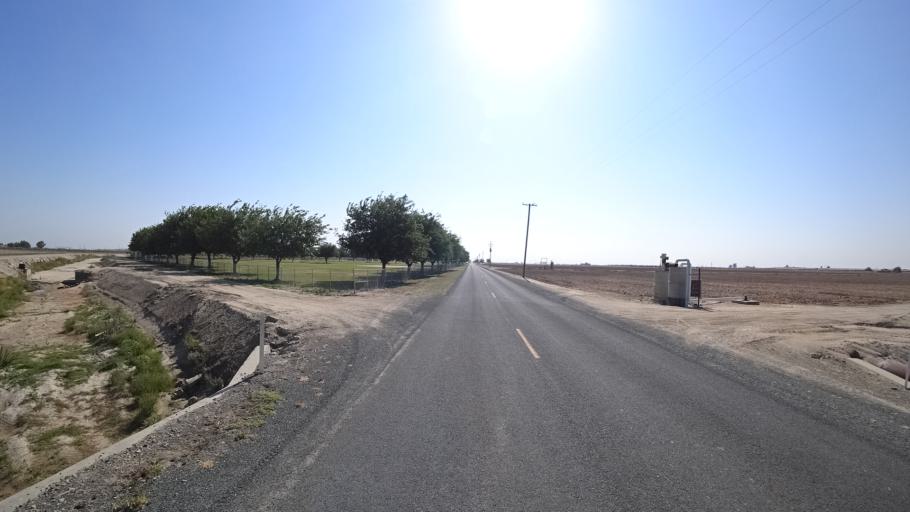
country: US
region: California
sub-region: Kings County
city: Home Garden
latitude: 36.2404
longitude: -119.6253
